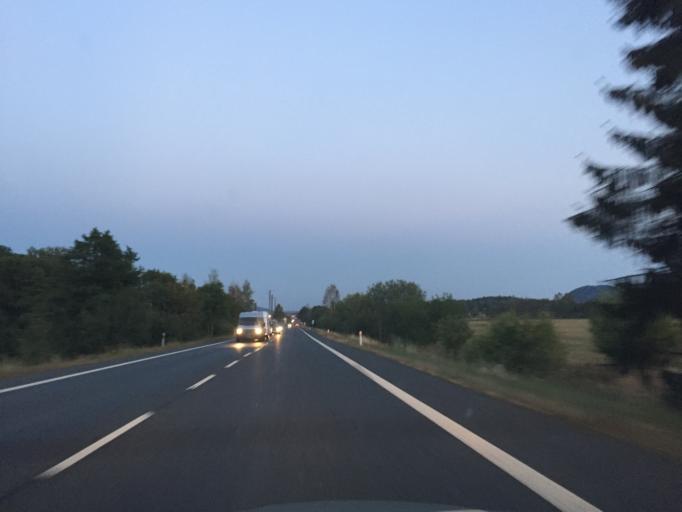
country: CZ
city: Cvikov
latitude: 50.7872
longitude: 14.6096
